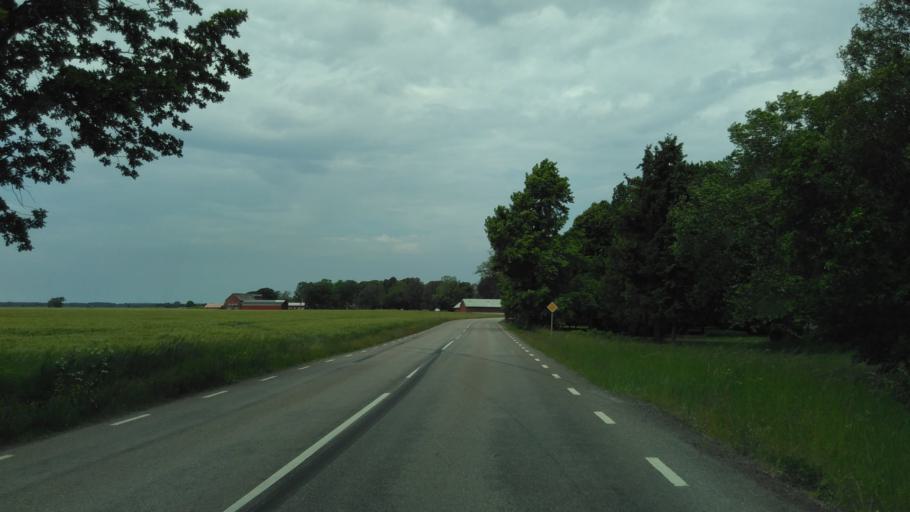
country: SE
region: Vaestra Goetaland
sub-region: Lidkopings Kommun
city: Lidkoping
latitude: 58.4633
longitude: 13.1516
